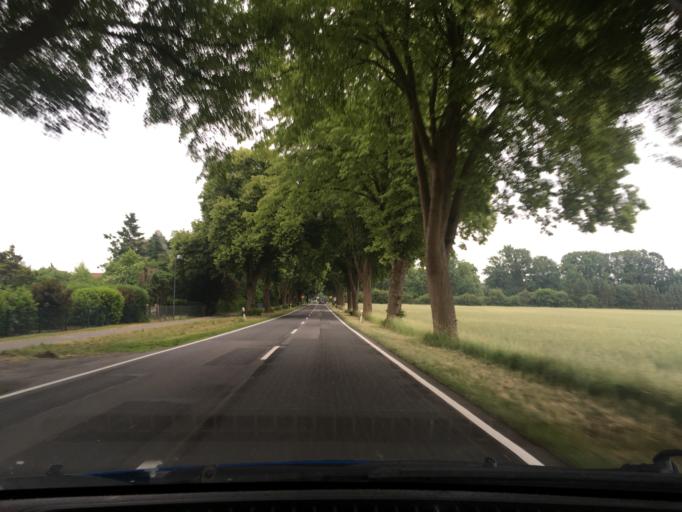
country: DE
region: Lower Saxony
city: Dahlenburg
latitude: 53.1889
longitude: 10.7243
